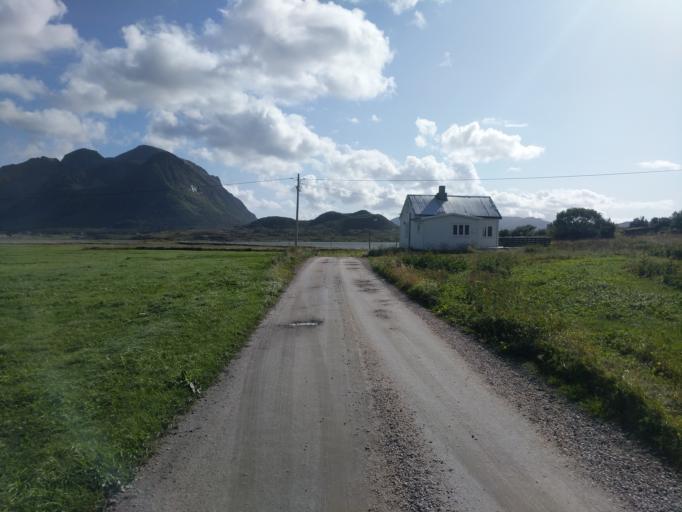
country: NO
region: Nordland
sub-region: Vestvagoy
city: Evjen
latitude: 68.3355
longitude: 13.8868
